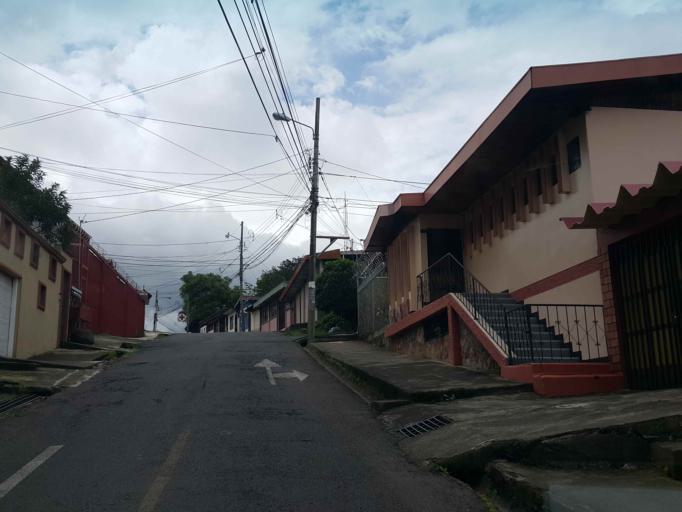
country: CR
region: Heredia
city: Mercedes
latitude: 10.0214
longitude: -84.1227
